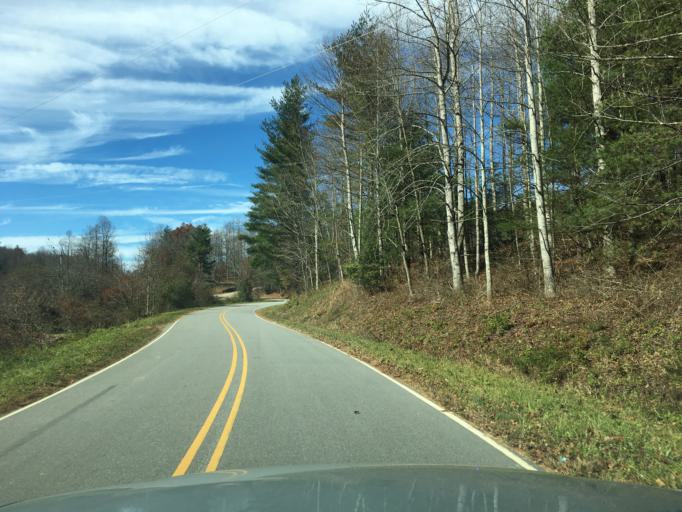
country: US
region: North Carolina
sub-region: Henderson County
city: Valley Hill
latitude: 35.2274
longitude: -82.5005
